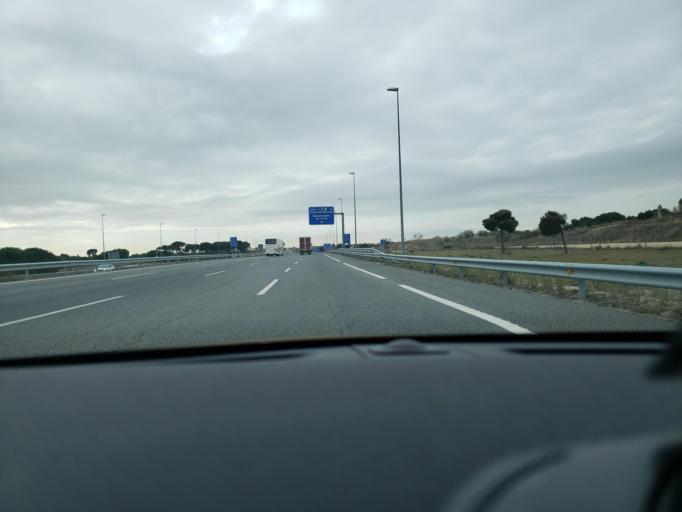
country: ES
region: Madrid
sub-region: Provincia de Madrid
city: Navalcarnero
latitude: 40.2624
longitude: -4.0427
